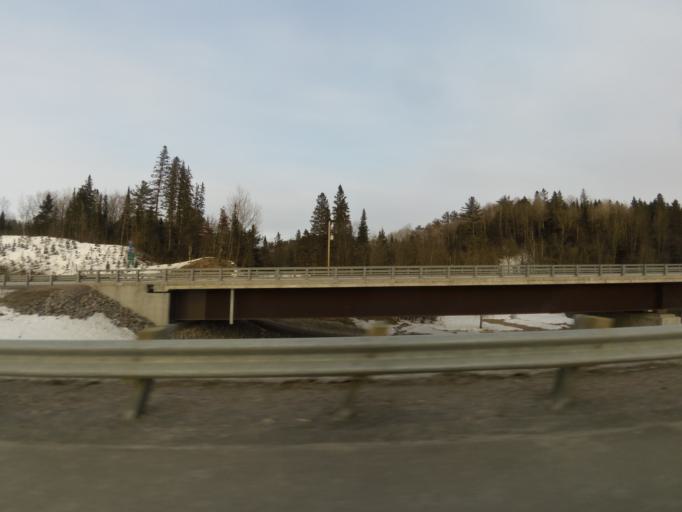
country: CA
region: Quebec
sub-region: Outaouais
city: Wakefield
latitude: 45.6330
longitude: -75.9405
